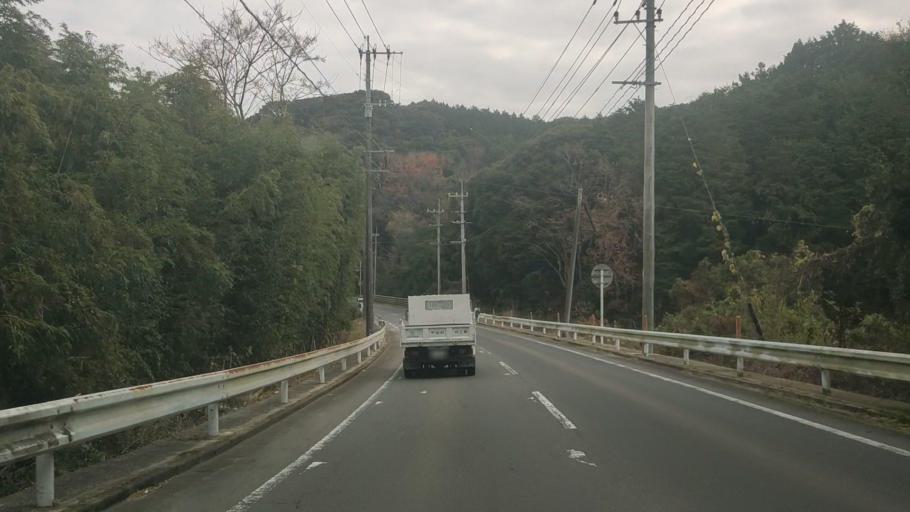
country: JP
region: Nagasaki
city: Shimabara
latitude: 32.8519
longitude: 130.2644
